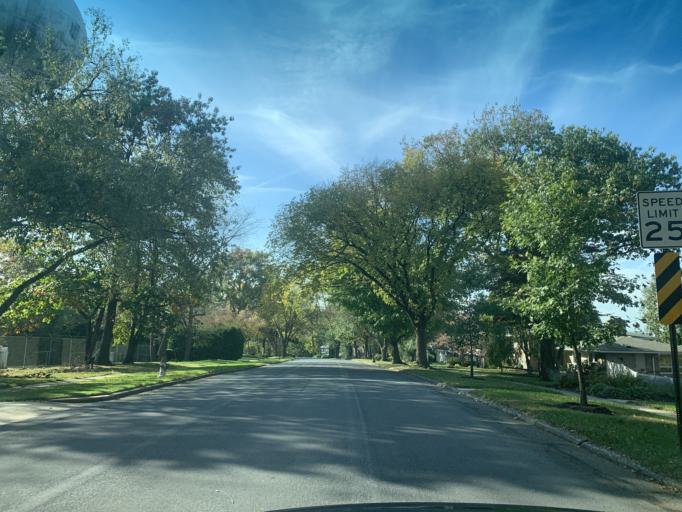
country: US
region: Pennsylvania
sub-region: Berks County
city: West Lawn
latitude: 40.3335
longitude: -75.9913
